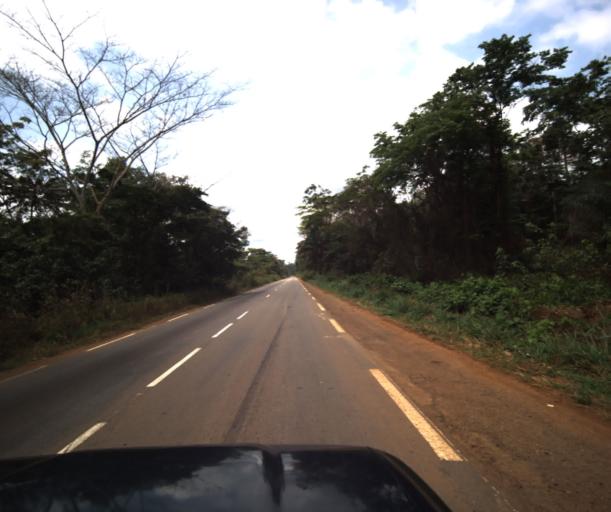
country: CM
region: Centre
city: Mbankomo
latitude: 3.7934
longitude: 11.3283
